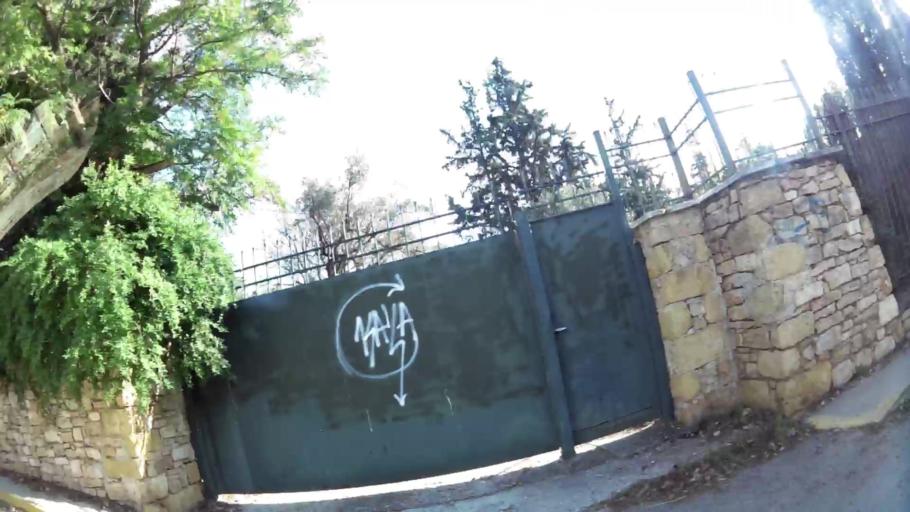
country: GR
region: Attica
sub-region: Nomarchia Athinas
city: Melissia
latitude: 38.0576
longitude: 23.8198
